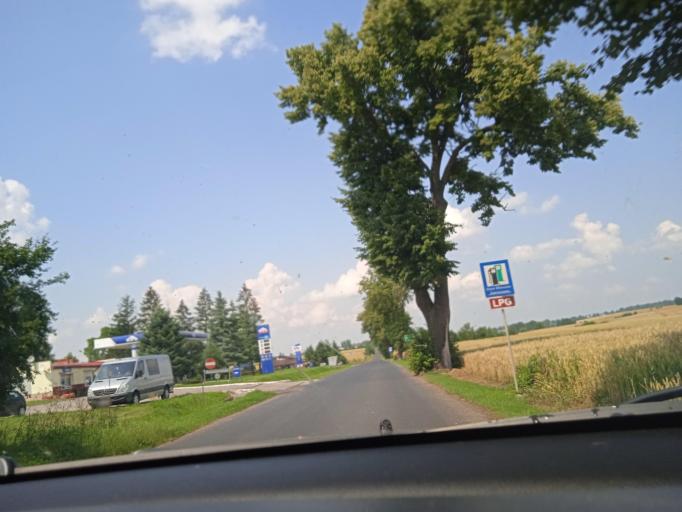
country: PL
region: Kujawsko-Pomorskie
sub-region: Powiat grudziadzki
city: Lasin
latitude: 53.5380
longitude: 19.0688
